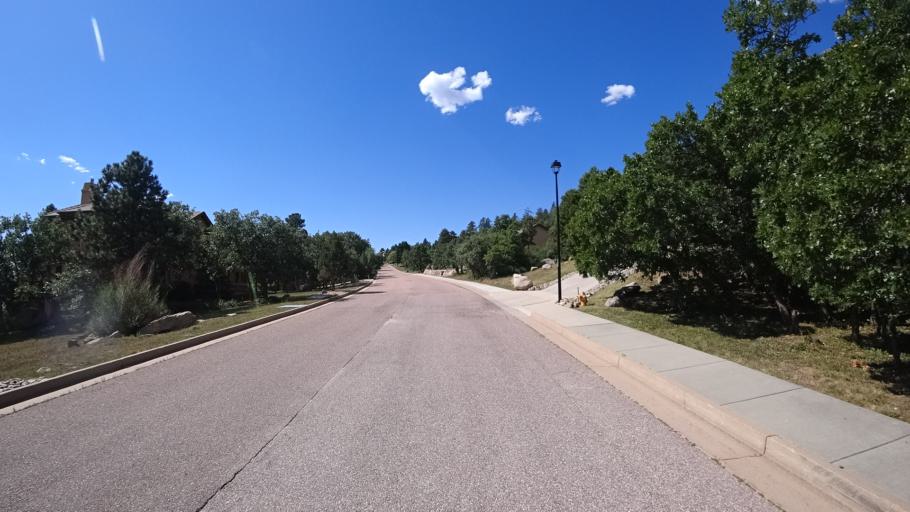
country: US
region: Colorado
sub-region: El Paso County
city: Fort Carson
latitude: 38.7447
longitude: -104.8364
